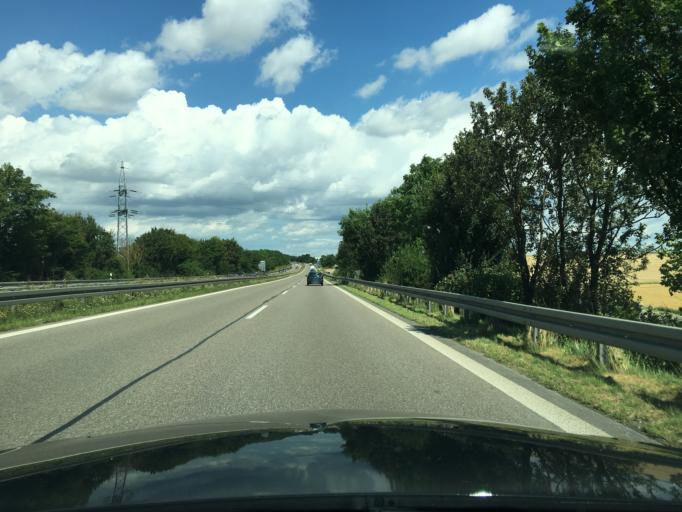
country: DE
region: Baden-Wuerttemberg
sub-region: Tuebingen Region
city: Dornstadt
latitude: 48.4439
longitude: 9.9725
